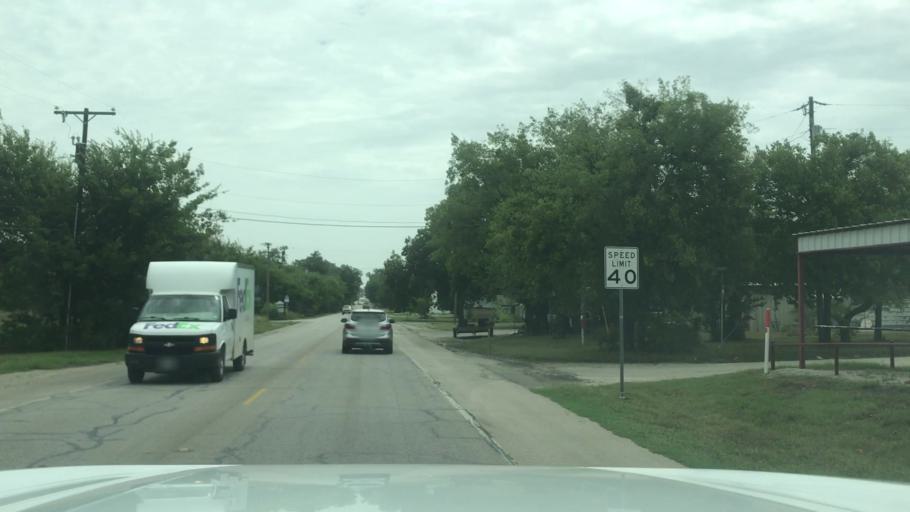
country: US
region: Texas
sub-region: Erath County
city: Dublin
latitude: 32.0874
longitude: -98.3518
